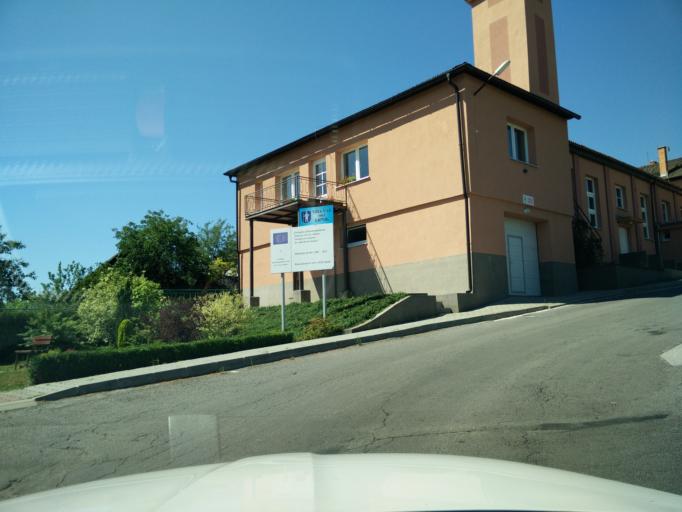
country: SK
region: Nitriansky
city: Handlova
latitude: 48.7789
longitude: 18.7097
